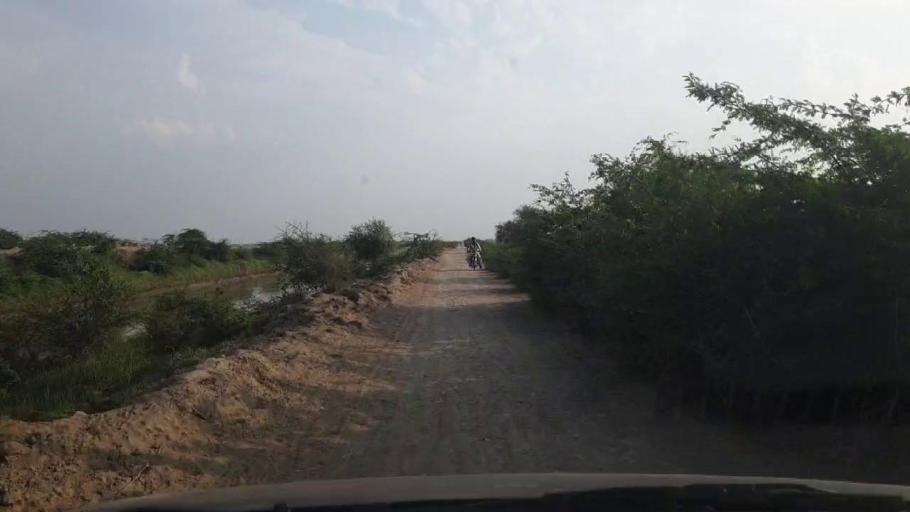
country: PK
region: Sindh
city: Badin
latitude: 24.5639
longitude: 68.6678
